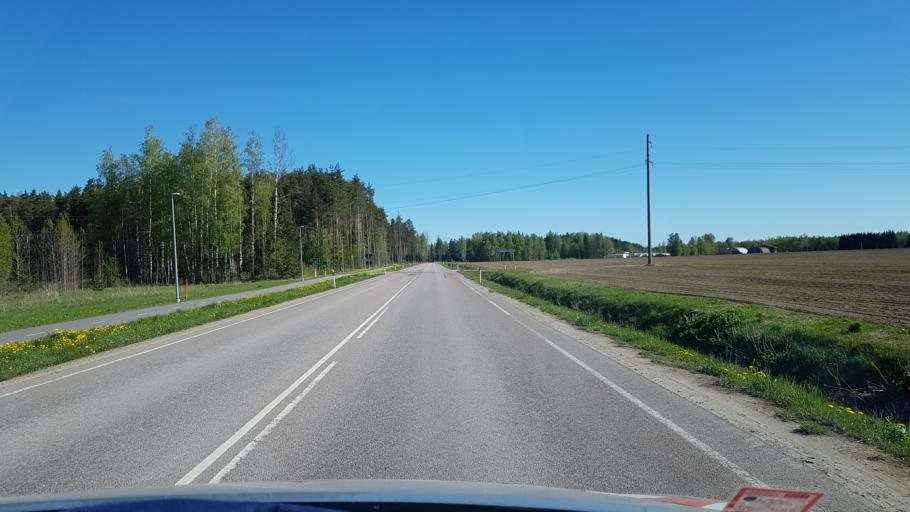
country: EE
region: Polvamaa
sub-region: Polva linn
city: Polva
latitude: 58.0905
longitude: 27.0926
